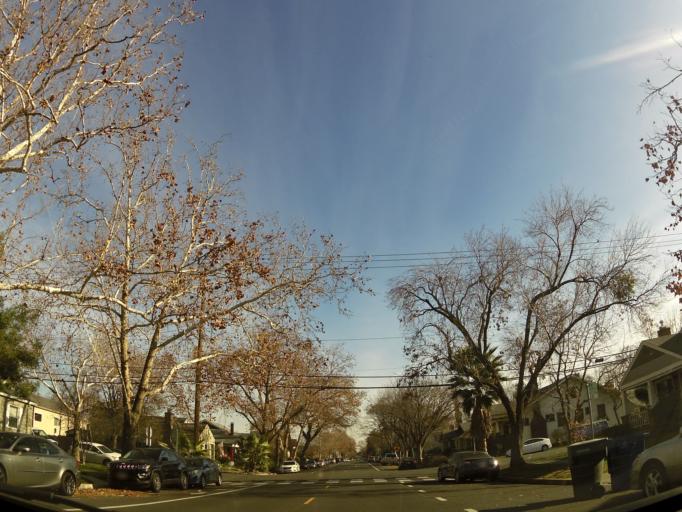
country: US
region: California
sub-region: Sacramento County
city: Sacramento
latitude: 38.5640
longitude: -121.4785
